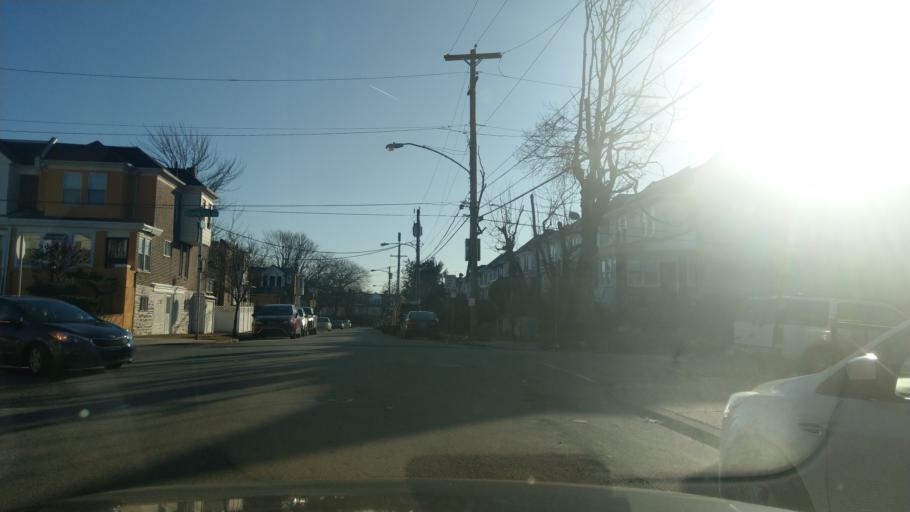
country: US
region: Pennsylvania
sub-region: Montgomery County
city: Wyncote
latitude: 40.0452
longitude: -75.1520
